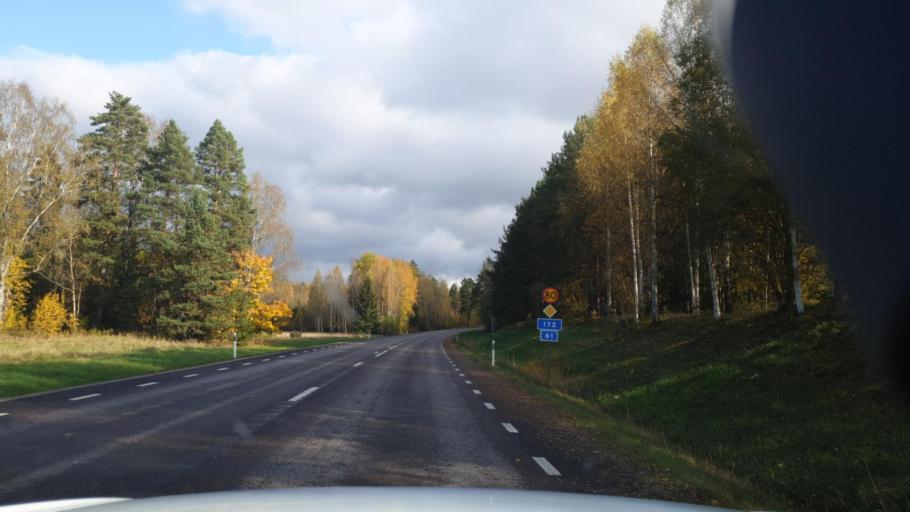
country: SE
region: Vaermland
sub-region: Arvika Kommun
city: Arvika
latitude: 59.6673
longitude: 12.5711
